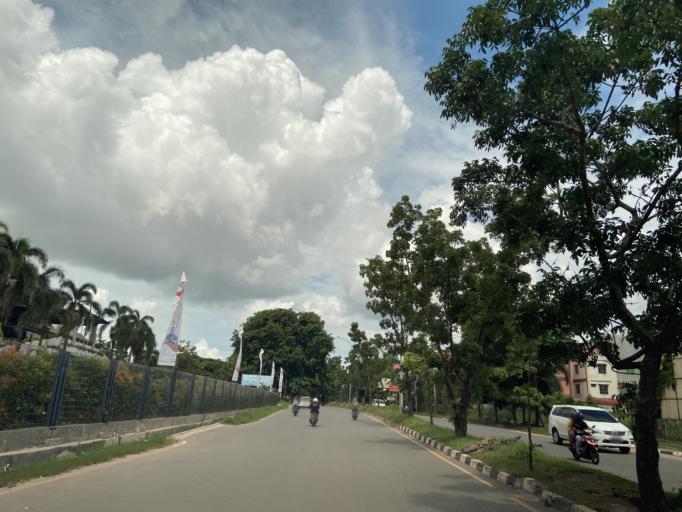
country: SG
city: Singapore
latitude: 1.1513
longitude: 104.0030
